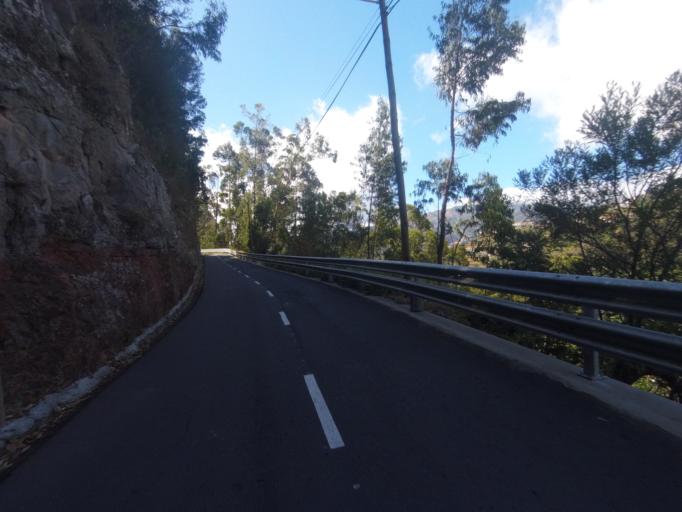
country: PT
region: Madeira
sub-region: Ribeira Brava
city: Campanario
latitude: 32.6872
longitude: -17.0323
